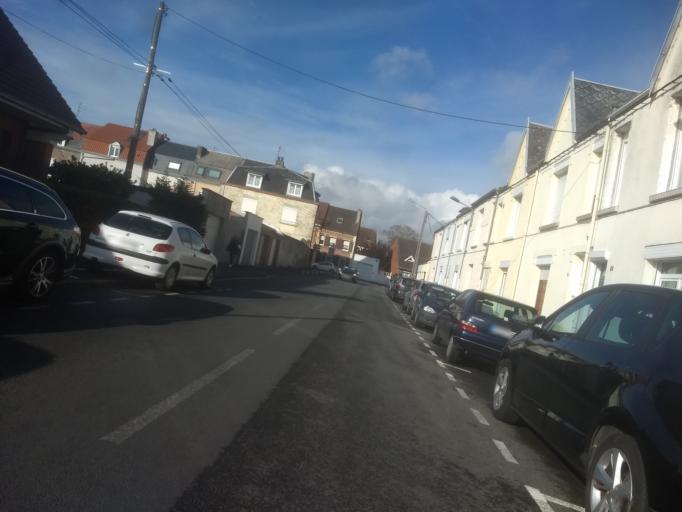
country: FR
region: Nord-Pas-de-Calais
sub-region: Departement du Pas-de-Calais
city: Arras
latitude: 50.2788
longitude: 2.7840
